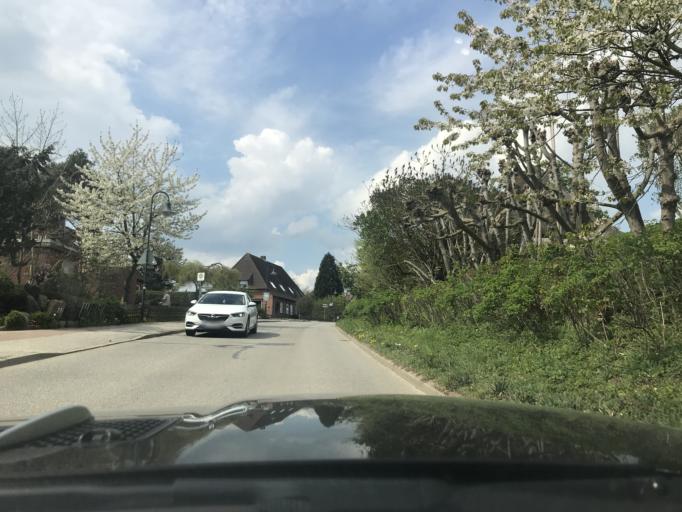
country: DE
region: Schleswig-Holstein
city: Schashagen
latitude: 54.0989
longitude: 10.8832
